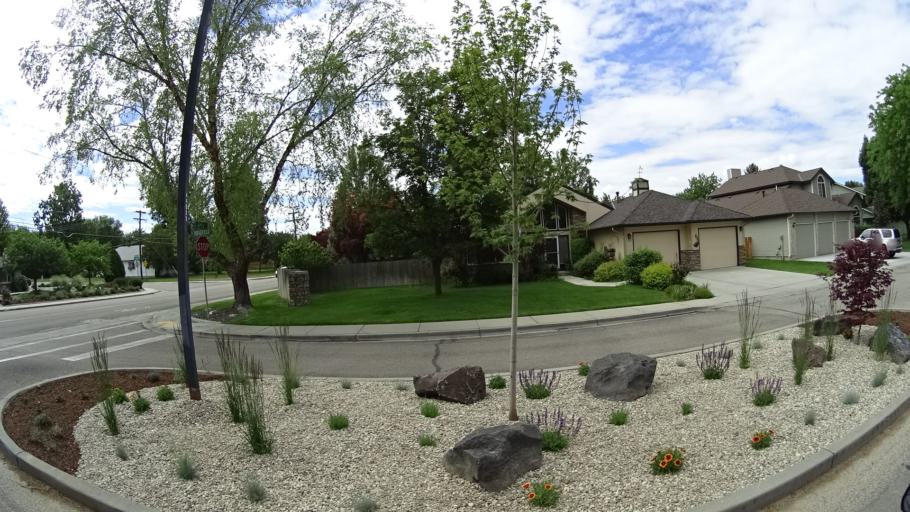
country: US
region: Idaho
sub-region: Ada County
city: Boise
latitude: 43.5719
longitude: -116.1737
